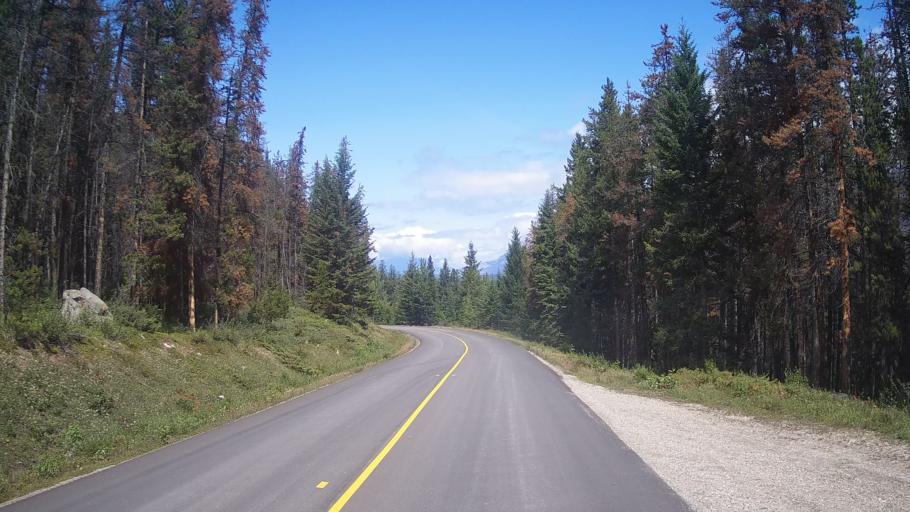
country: CA
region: Alberta
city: Jasper Park Lodge
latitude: 52.7851
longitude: -118.0327
